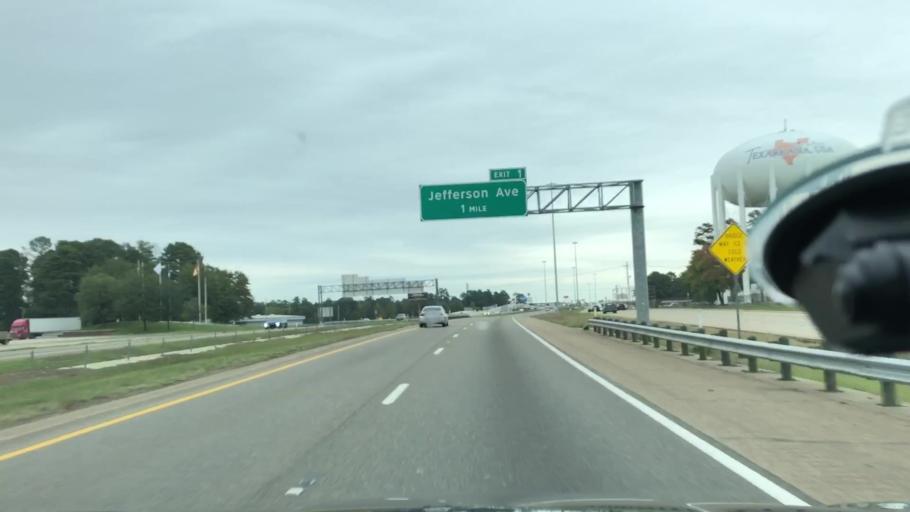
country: US
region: Arkansas
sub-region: Miller County
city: Texarkana
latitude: 33.4692
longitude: -94.0562
